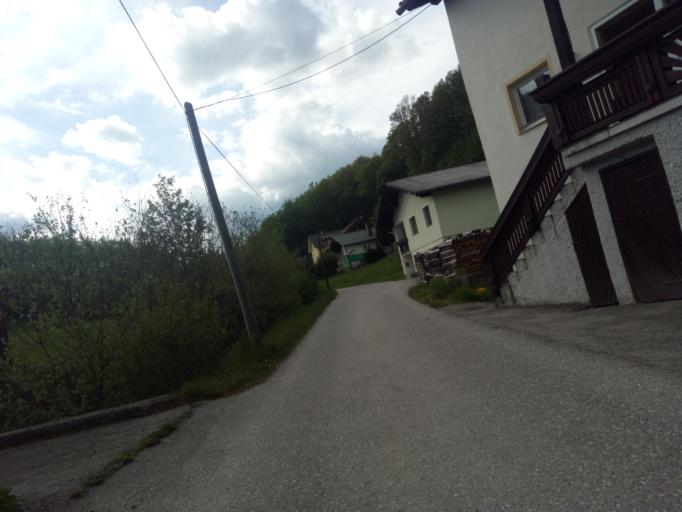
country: AT
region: Lower Austria
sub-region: Politischer Bezirk Wien-Umgebung
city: Wolfsgraben
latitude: 48.1277
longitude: 16.0850
